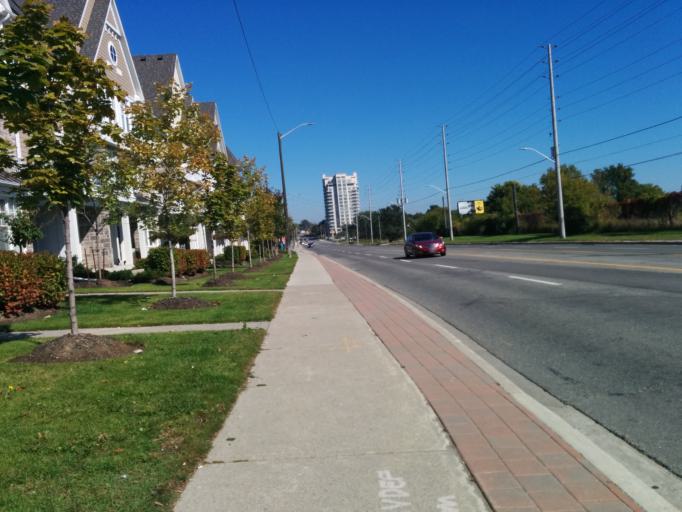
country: CA
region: Ontario
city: Etobicoke
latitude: 43.5860
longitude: -79.5493
